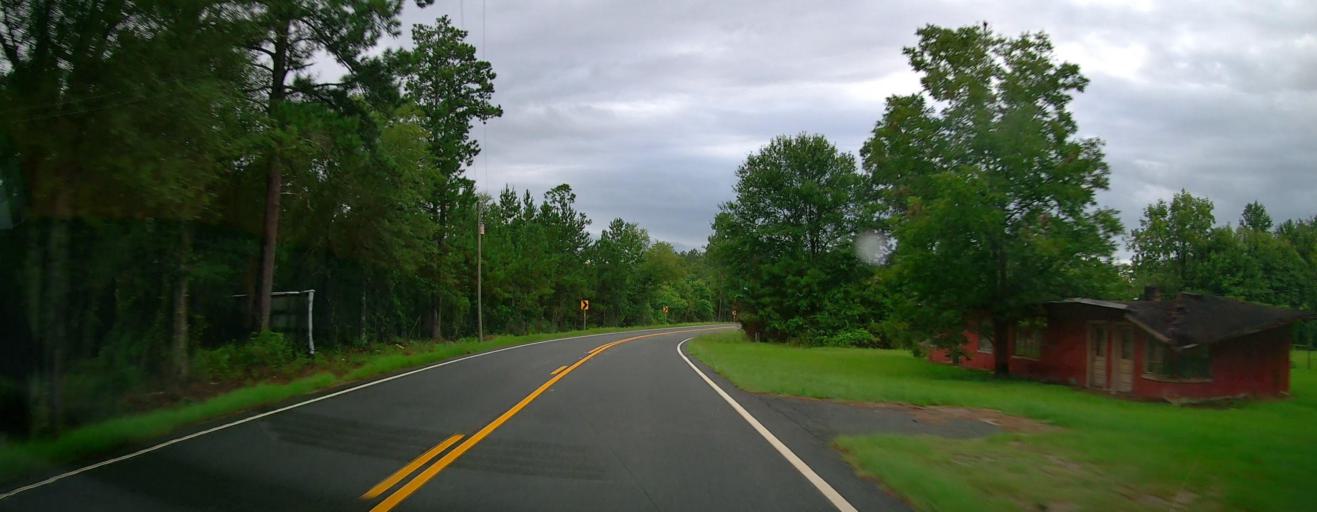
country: US
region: Georgia
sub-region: Ware County
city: Deenwood
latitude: 31.2723
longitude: -82.4123
